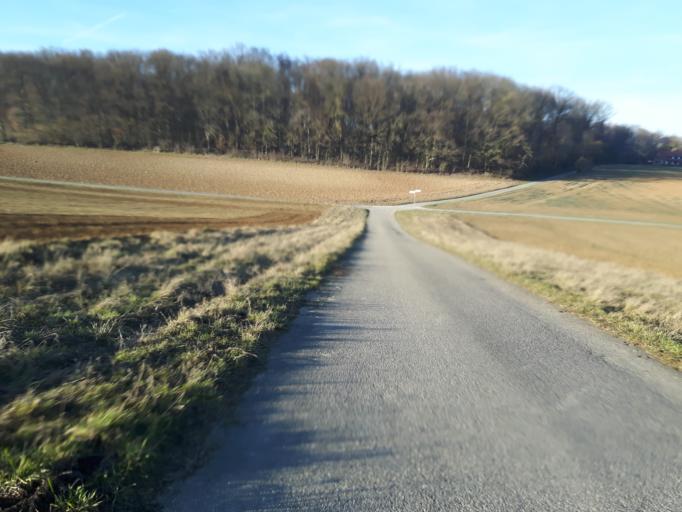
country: DE
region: Baden-Wuerttemberg
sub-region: Regierungsbezirk Stuttgart
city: Leingarten
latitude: 49.1603
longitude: 9.0969
